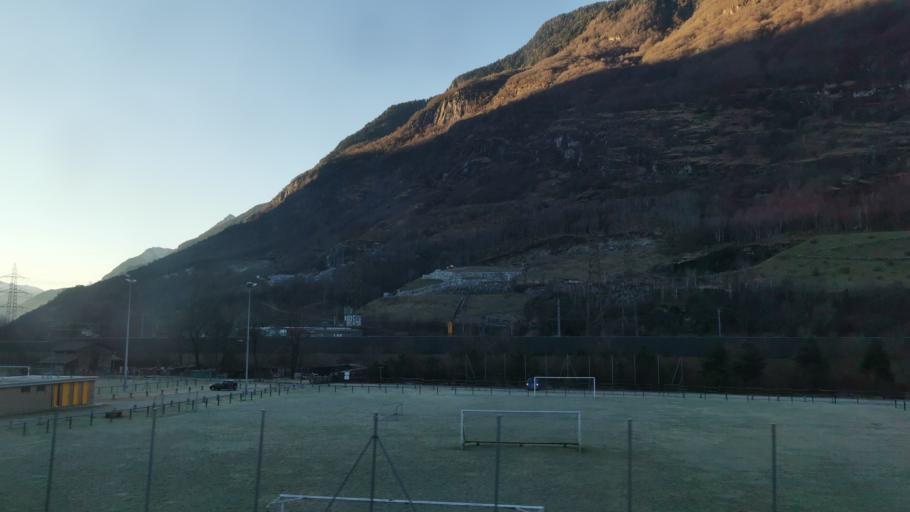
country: CH
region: Ticino
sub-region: Riviera District
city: Biasca
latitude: 46.3605
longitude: 8.9528
